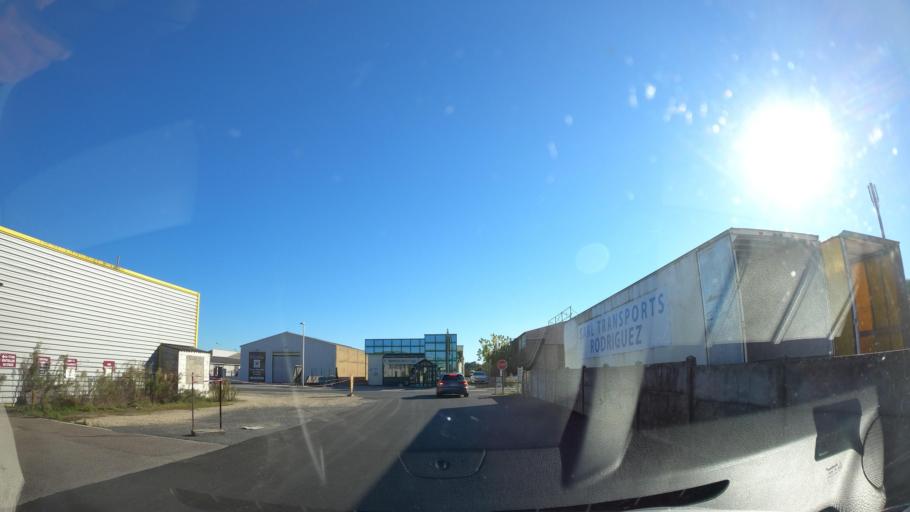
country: FR
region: Aquitaine
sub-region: Departement de la Dordogne
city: Cours-de-Pile
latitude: 44.8494
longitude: 0.5367
